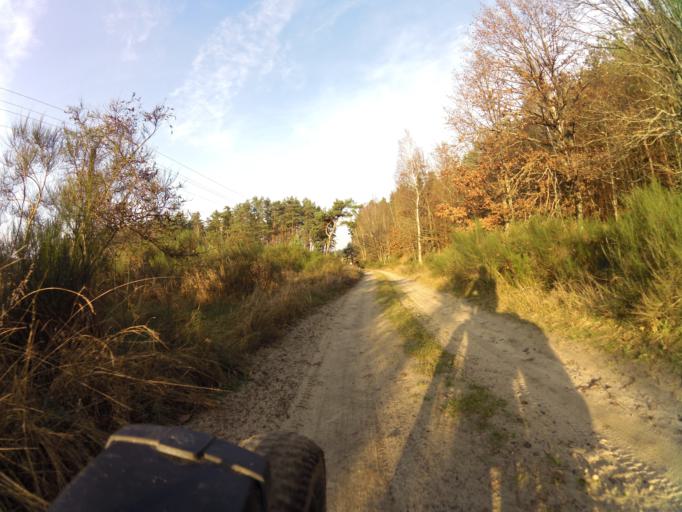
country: PL
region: West Pomeranian Voivodeship
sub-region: Powiat koszalinski
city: Polanow
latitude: 54.0995
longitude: 16.6482
